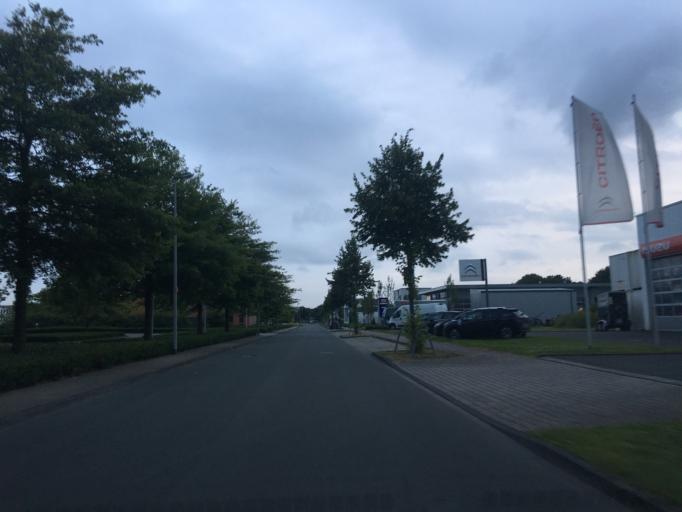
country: DE
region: North Rhine-Westphalia
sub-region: Regierungsbezirk Munster
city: Muenster
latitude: 51.9327
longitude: 7.6538
